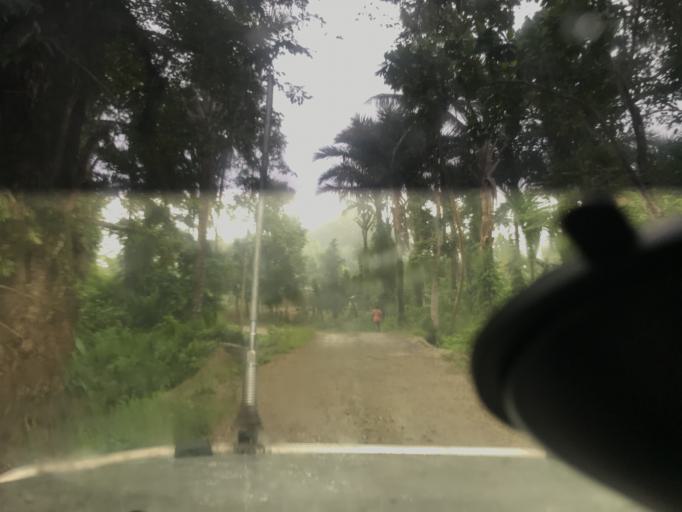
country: SB
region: Choiseul
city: Taro'a
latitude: -9.1886
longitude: 160.9440
